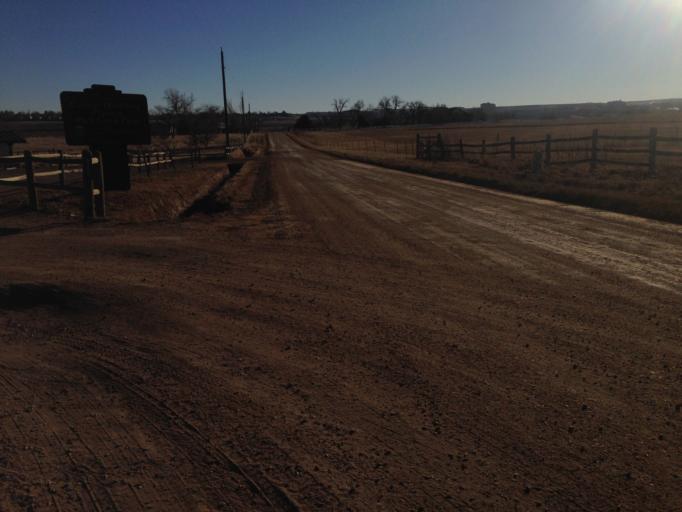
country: US
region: Colorado
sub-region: Broomfield County
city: Broomfield
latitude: 39.9473
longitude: -105.1093
